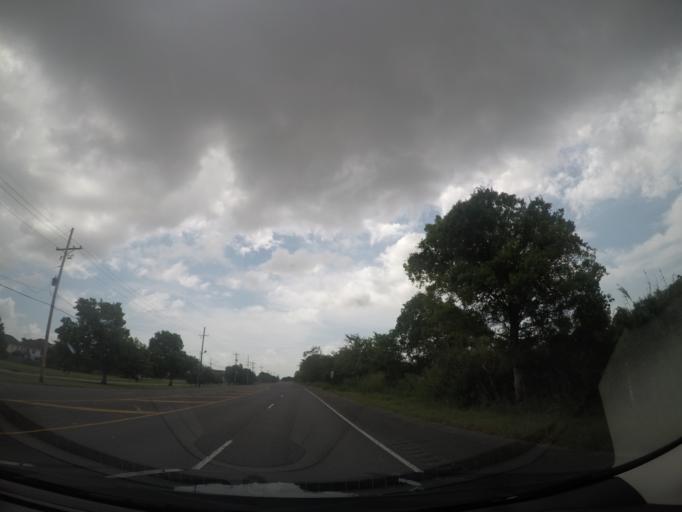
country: US
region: Louisiana
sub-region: Saint Tammany Parish
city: Eden Isle
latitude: 30.0651
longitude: -89.8154
